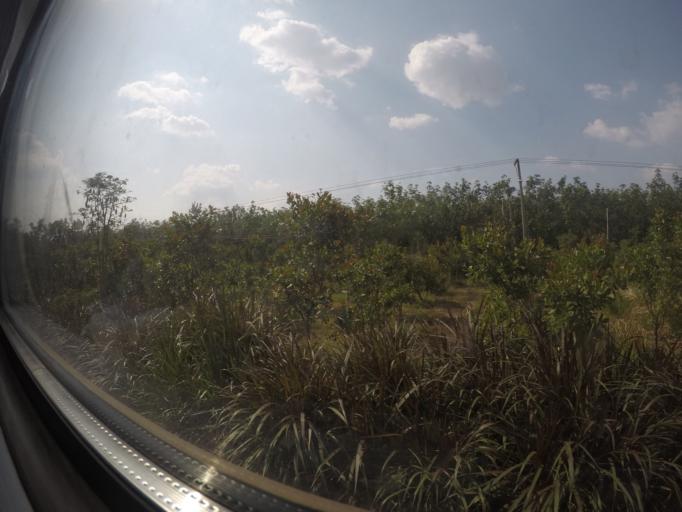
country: VN
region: Dong Nai
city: Long Khanh
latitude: 10.9289
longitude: 107.2006
